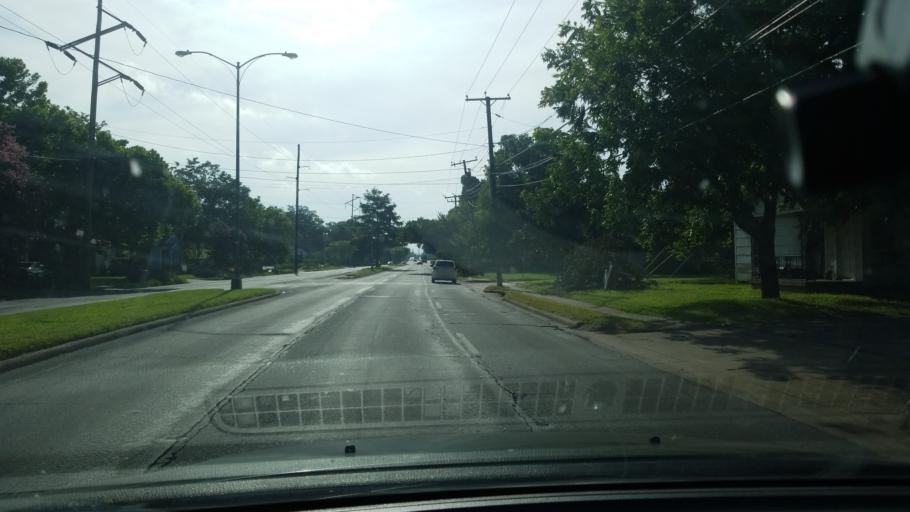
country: US
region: Texas
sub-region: Dallas County
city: Balch Springs
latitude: 32.7196
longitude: -96.6783
